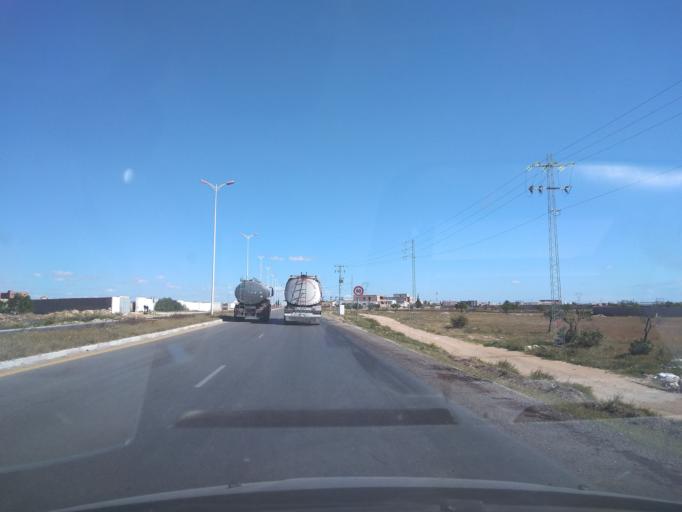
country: TN
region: Safaqis
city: Sfax
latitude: 34.8035
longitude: 10.6894
